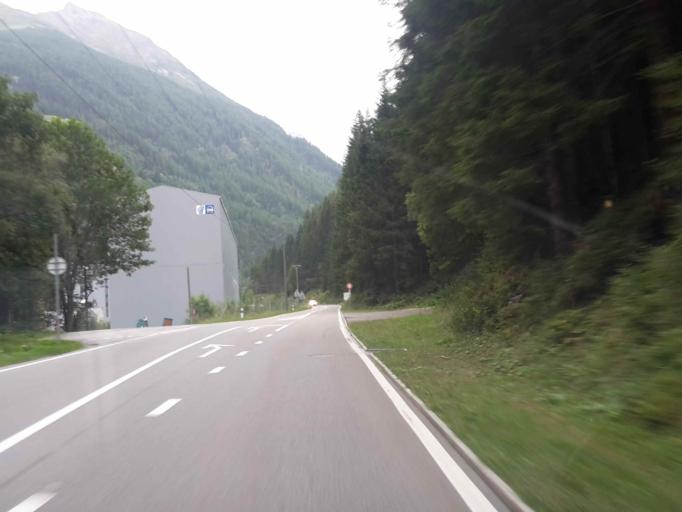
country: CH
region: Valais
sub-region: Saint-Maurice District
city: Salvan
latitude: 46.0648
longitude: 6.9887
